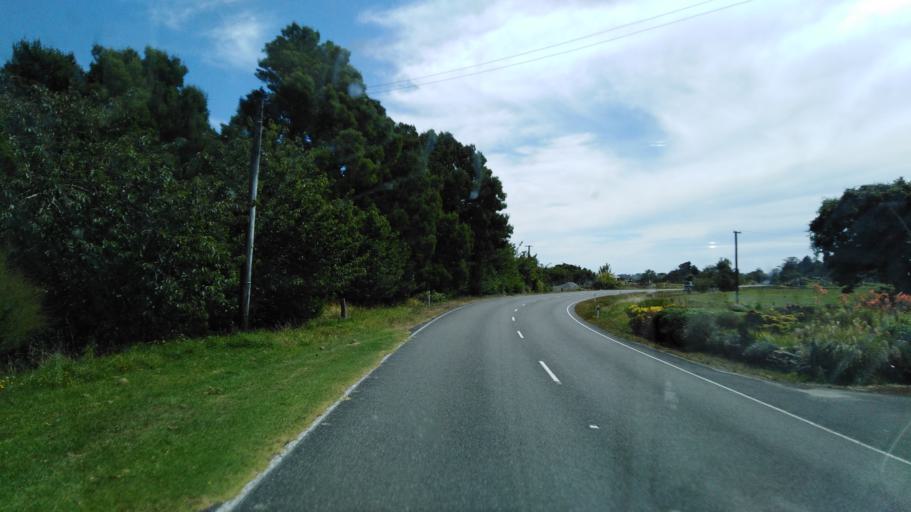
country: NZ
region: West Coast
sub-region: Buller District
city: Westport
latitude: -41.7564
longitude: 171.6335
